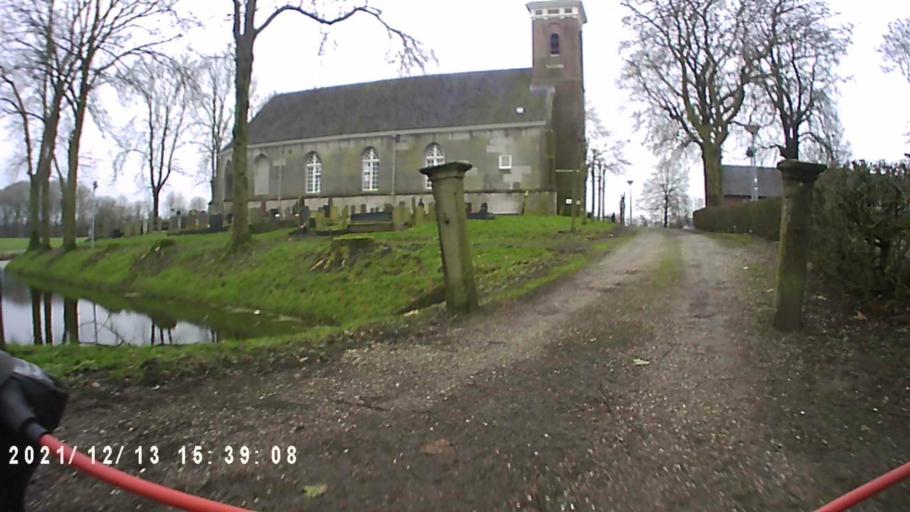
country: NL
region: Groningen
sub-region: Gemeente Appingedam
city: Appingedam
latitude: 53.3236
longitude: 6.8336
